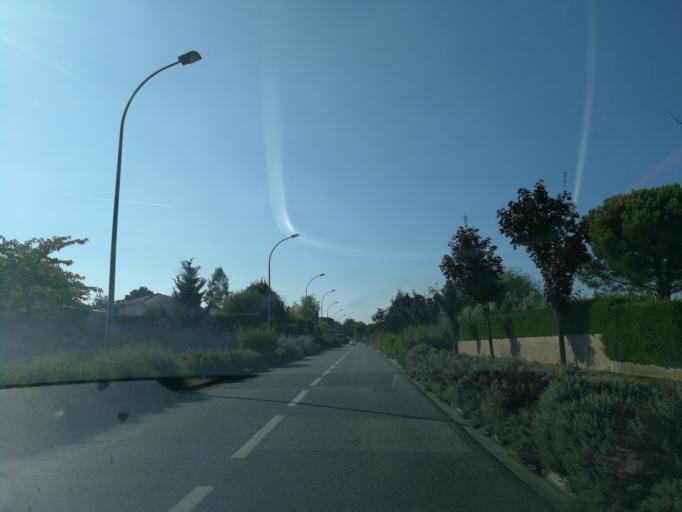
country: FR
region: Midi-Pyrenees
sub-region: Departement de la Haute-Garonne
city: Balma
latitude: 43.6193
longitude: 1.5164
